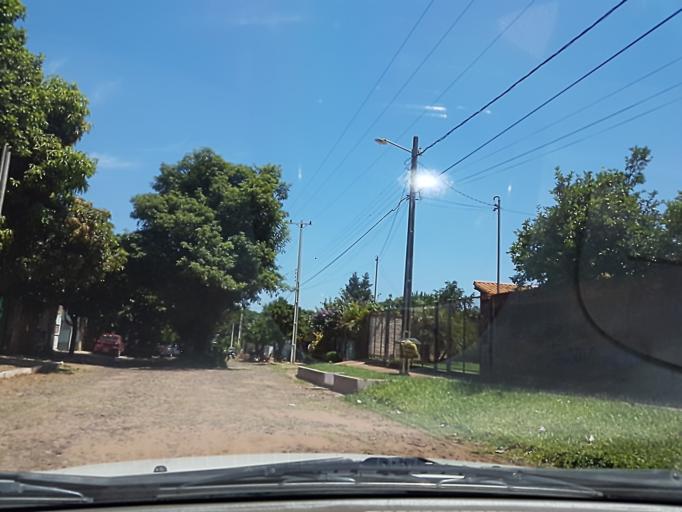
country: PY
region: Central
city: Fernando de la Mora
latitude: -25.2924
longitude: -57.5324
